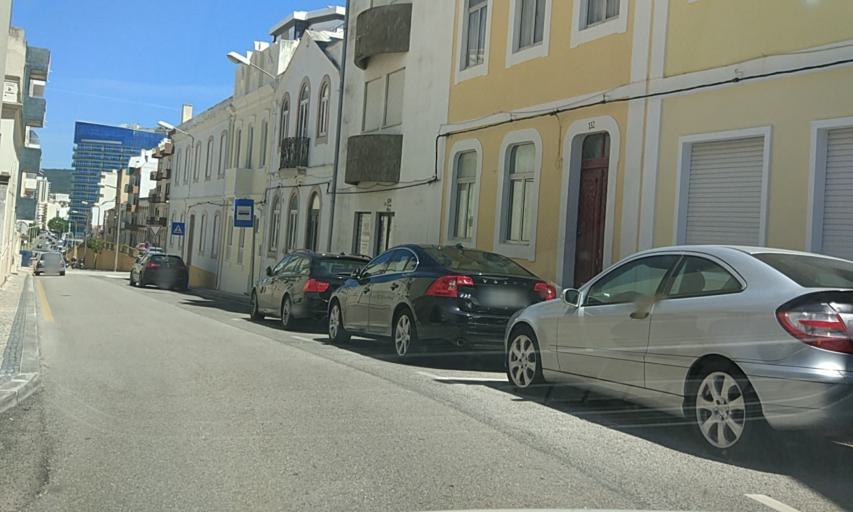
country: PT
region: Coimbra
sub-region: Figueira da Foz
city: Figueira da Foz
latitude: 40.1527
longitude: -8.8655
